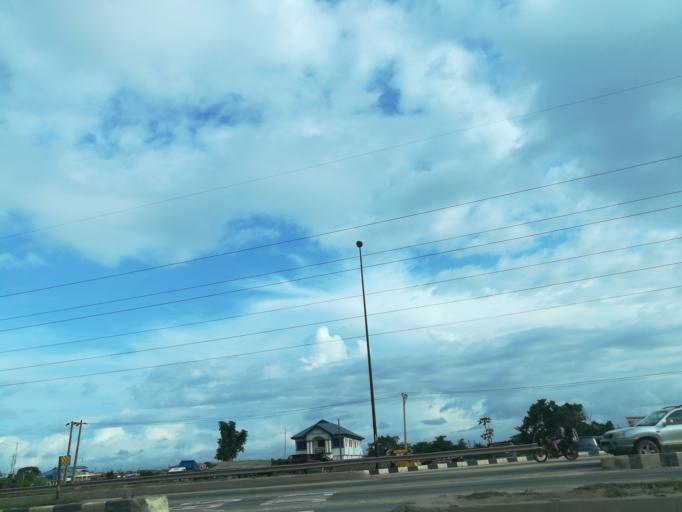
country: NG
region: Lagos
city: Ebute Ikorodu
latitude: 6.6190
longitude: 3.4685
